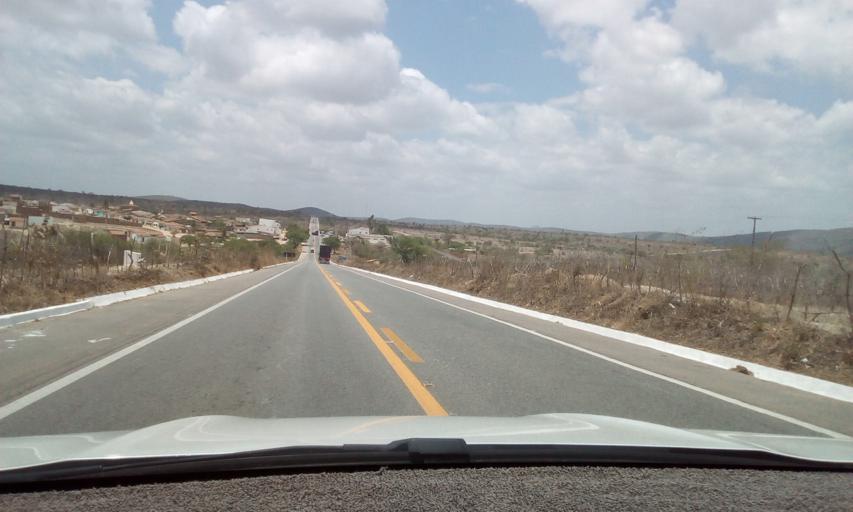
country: BR
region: Pernambuco
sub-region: Taquaritinga Do Norte
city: Taquaritinga do Norte
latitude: -7.7335
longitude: -36.0768
